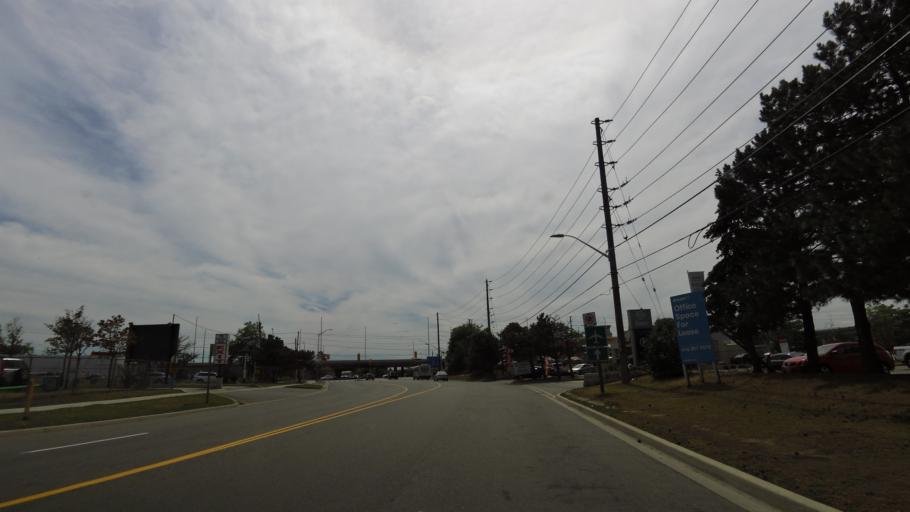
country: CA
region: Ontario
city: Etobicoke
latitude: 43.6872
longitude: -79.6069
